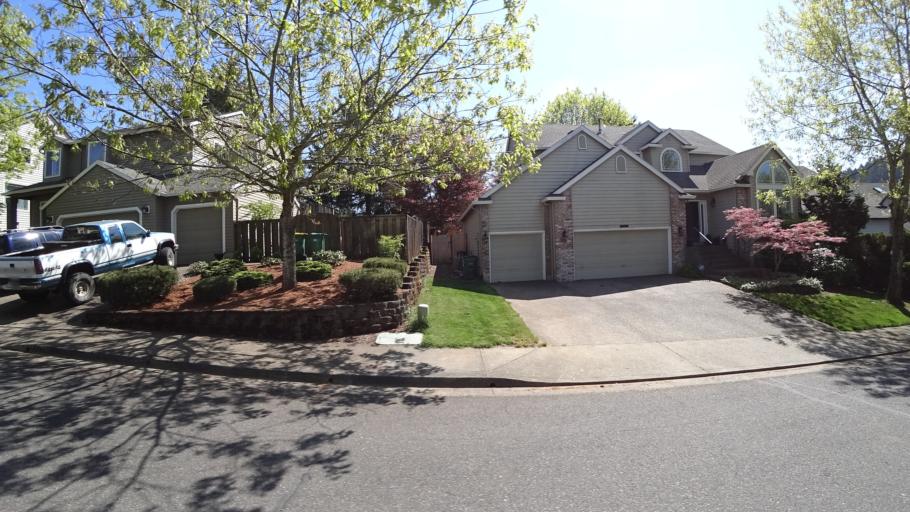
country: US
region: Oregon
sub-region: Washington County
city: King City
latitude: 45.4282
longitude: -122.8368
